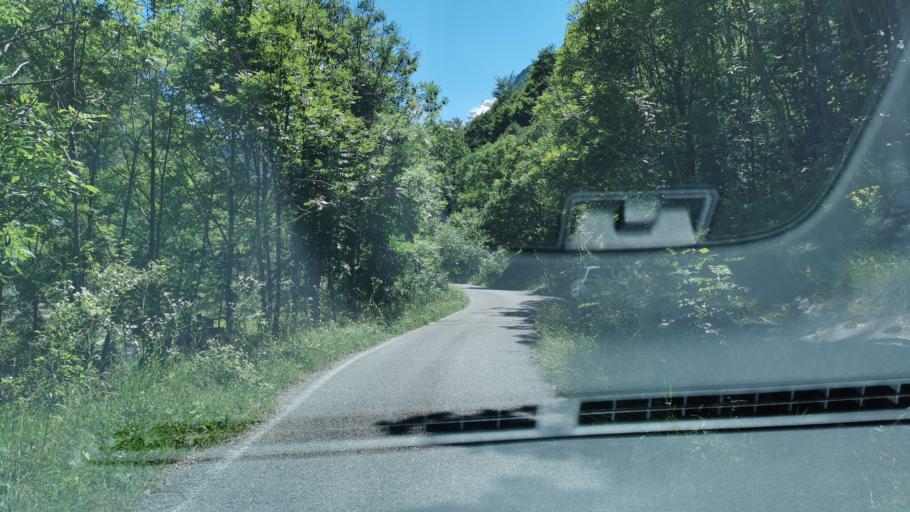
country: IT
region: Piedmont
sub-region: Provincia di Cuneo
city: Entracque
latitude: 44.1962
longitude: 7.3834
